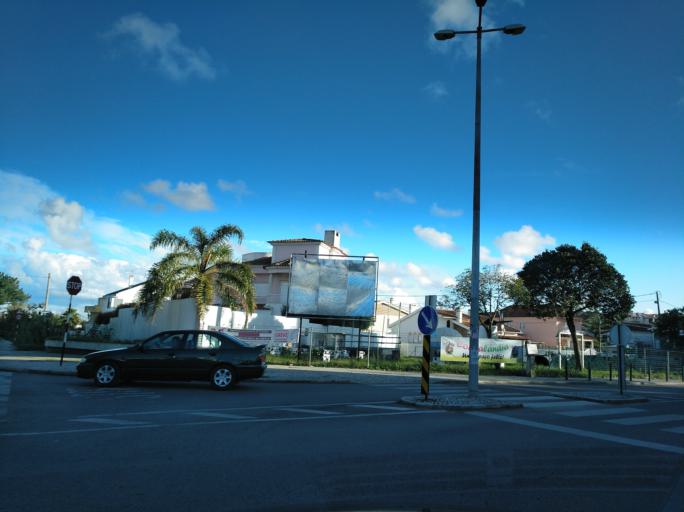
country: PT
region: Setubal
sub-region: Almada
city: Sobreda
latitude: 38.6486
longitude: -9.1833
